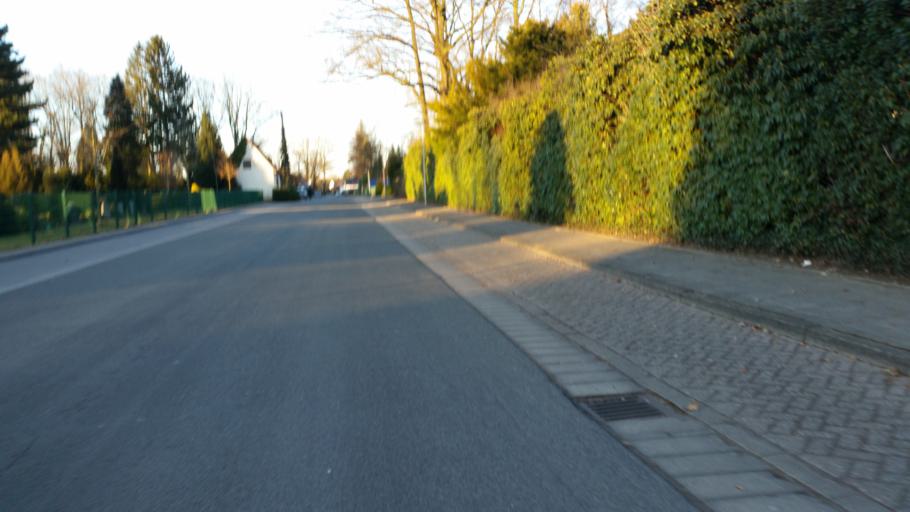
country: DE
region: North Rhine-Westphalia
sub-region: Regierungsbezirk Munster
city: Rheine
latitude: 52.2854
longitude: 7.4092
